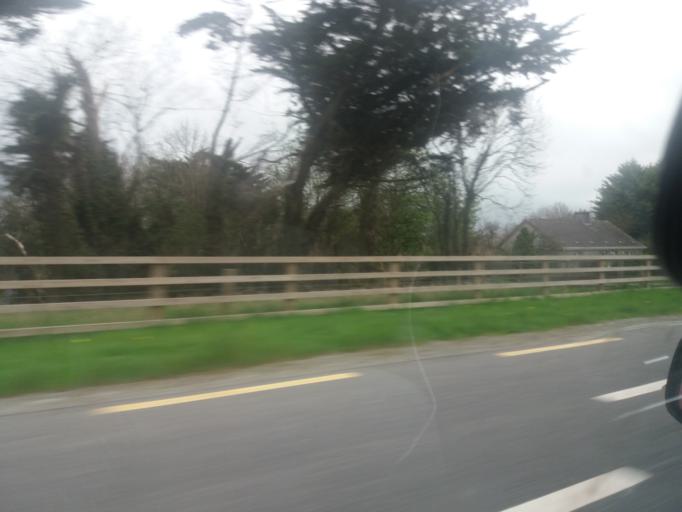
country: IE
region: Munster
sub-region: County Limerick
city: Rathkeale
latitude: 52.5020
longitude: -8.9923
